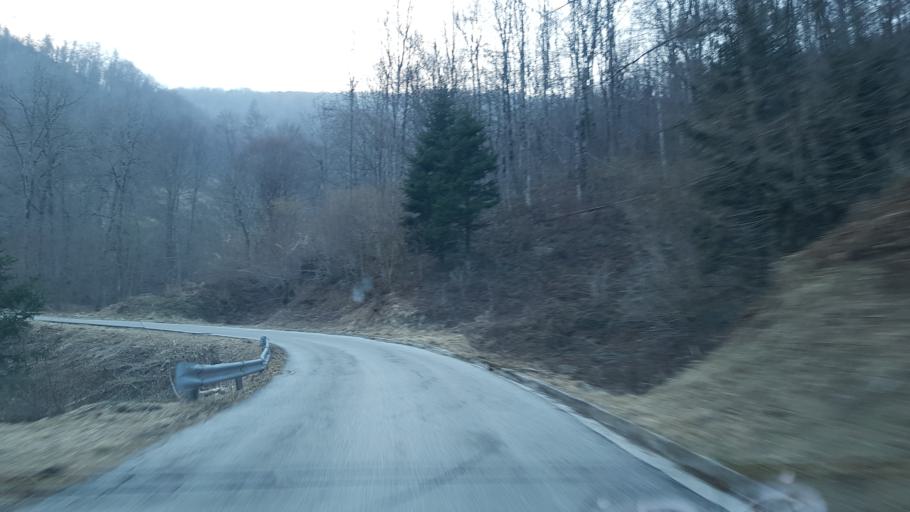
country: IT
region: Friuli Venezia Giulia
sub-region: Provincia di Udine
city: Taipana
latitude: 46.2182
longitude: 13.3867
